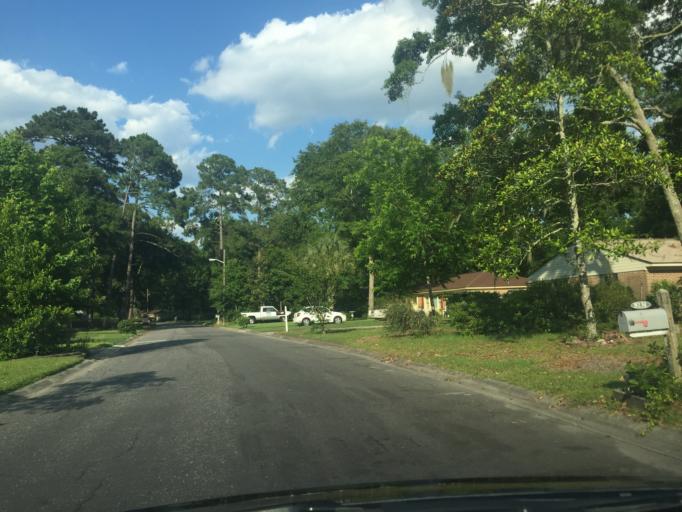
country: US
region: Georgia
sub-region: Chatham County
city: Montgomery
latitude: 31.9793
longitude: -81.1087
